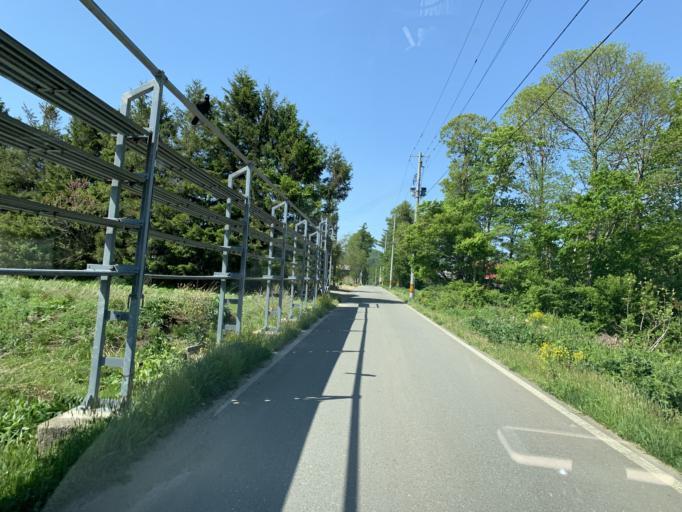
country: JP
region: Iwate
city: Shizukuishi
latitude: 39.5564
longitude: 140.8309
